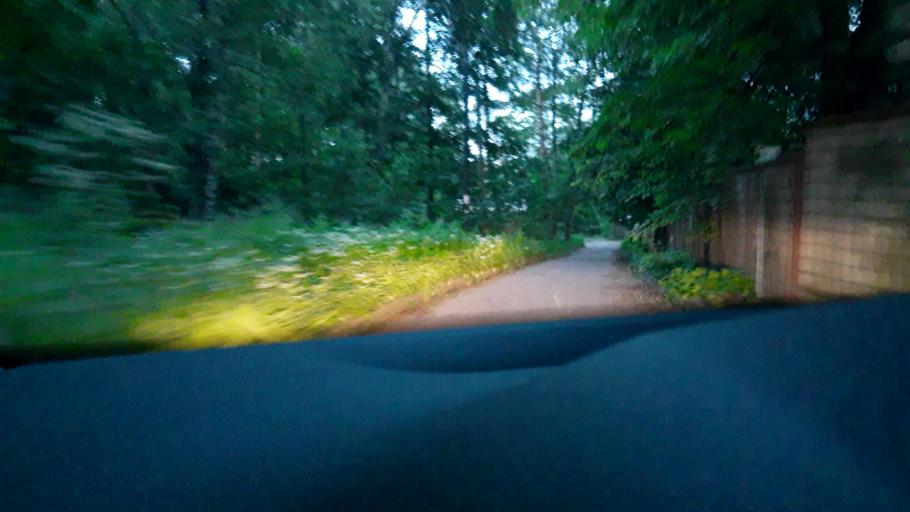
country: RU
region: Moscow
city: Khimki
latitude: 55.8766
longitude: 37.4358
